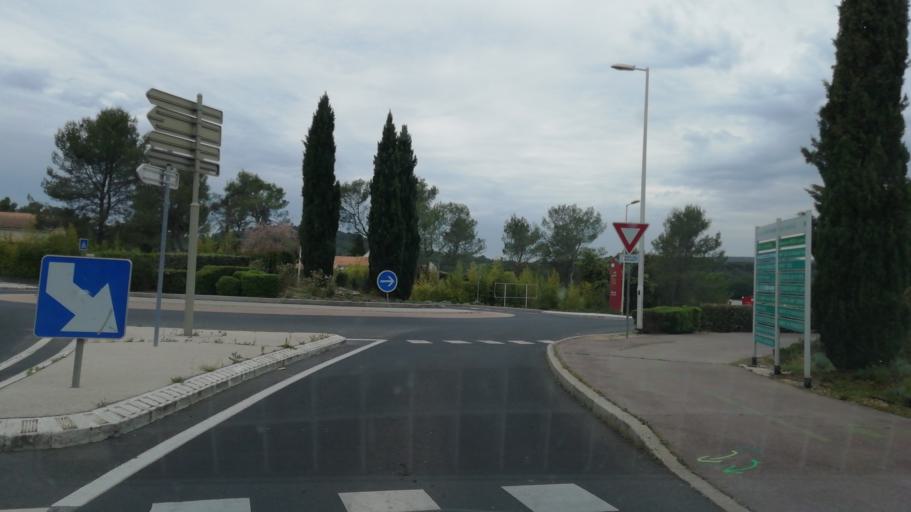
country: FR
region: Languedoc-Roussillon
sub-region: Departement de l'Herault
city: Saint-Clement-de-Riviere
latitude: 43.7073
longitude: 3.8309
